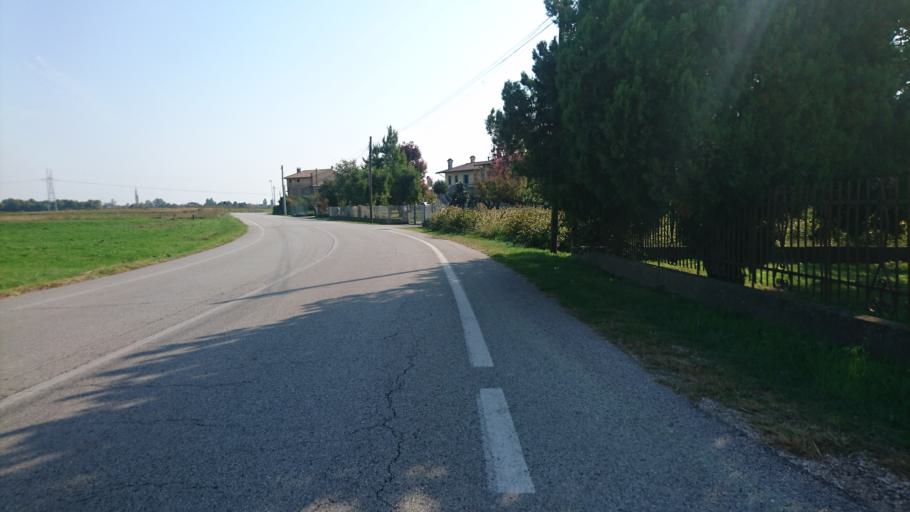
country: IT
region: Veneto
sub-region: Provincia di Vicenza
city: Grumolo delle Abbadesse
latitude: 45.5417
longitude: 11.6709
